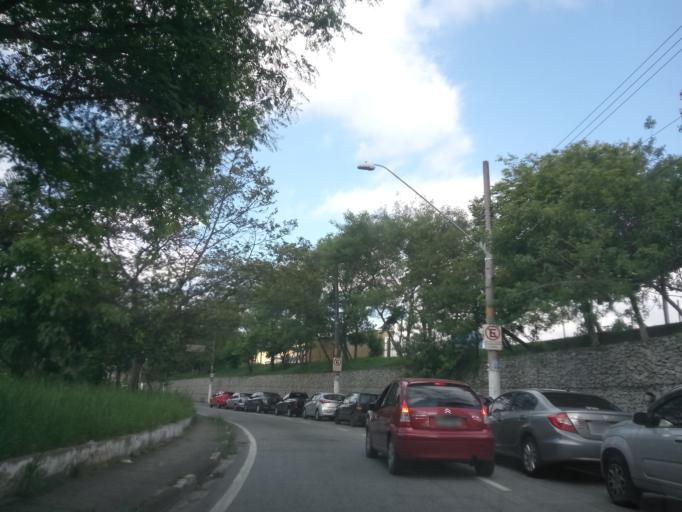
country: BR
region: Sao Paulo
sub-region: Sao Bernardo Do Campo
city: Sao Bernardo do Campo
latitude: -23.7291
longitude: -46.5683
